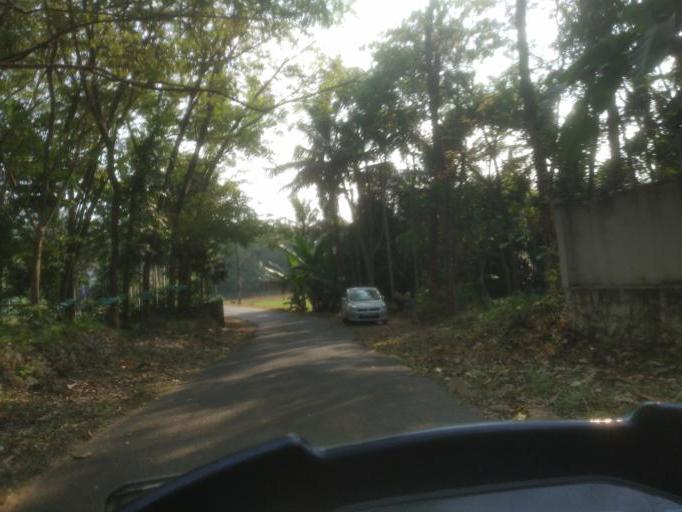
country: IN
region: Kerala
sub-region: Ernakulam
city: Piravam
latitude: 9.8409
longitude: 76.5252
